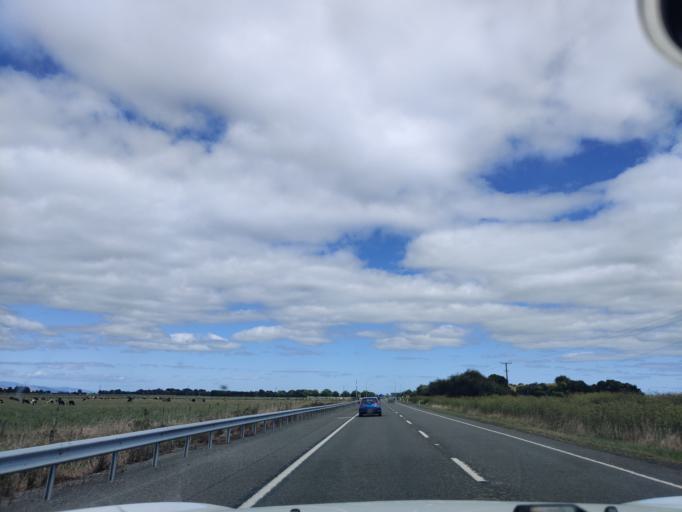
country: NZ
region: Manawatu-Wanganui
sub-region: Palmerston North City
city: Palmerston North
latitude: -40.4014
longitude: 175.5033
